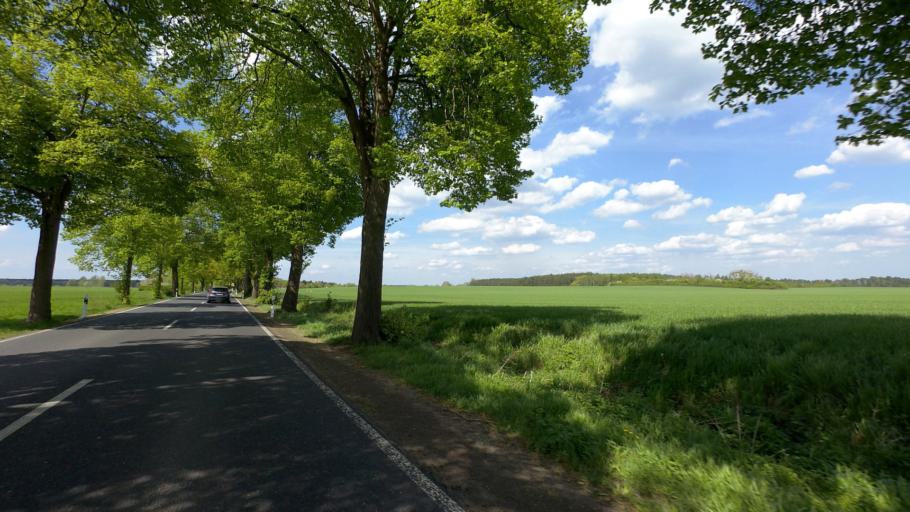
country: DE
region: Brandenburg
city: Marienwerder
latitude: 52.8927
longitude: 13.5406
